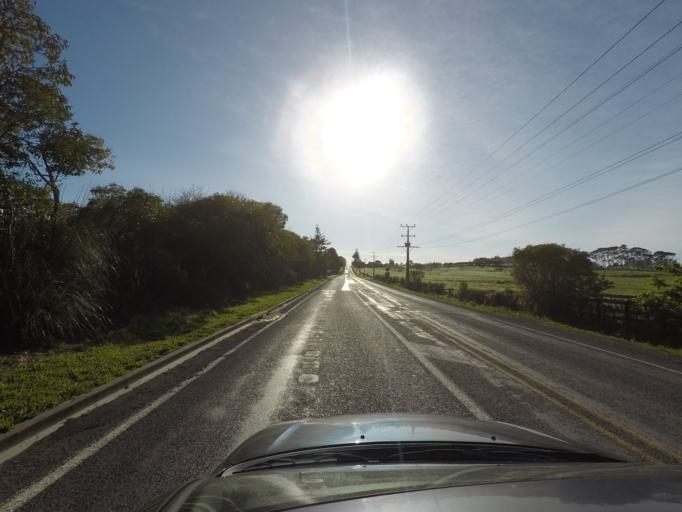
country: NZ
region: Auckland
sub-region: Auckland
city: Red Hill
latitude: -36.9984
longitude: 174.9693
